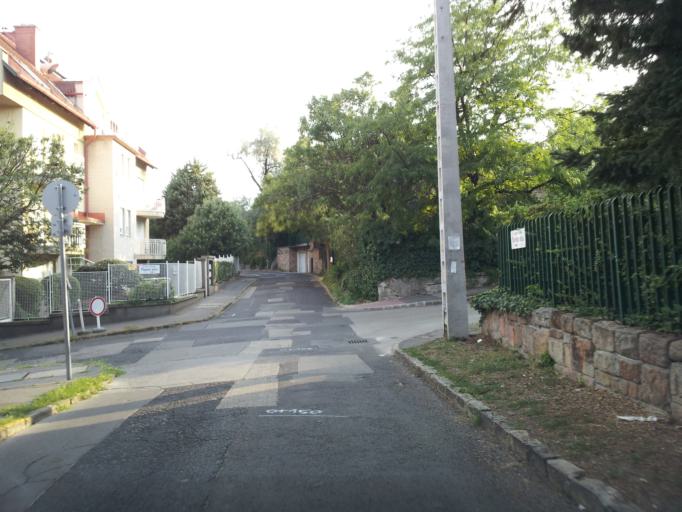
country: HU
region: Budapest
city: Budapest XII. keruelet
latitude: 47.4939
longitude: 19.0087
